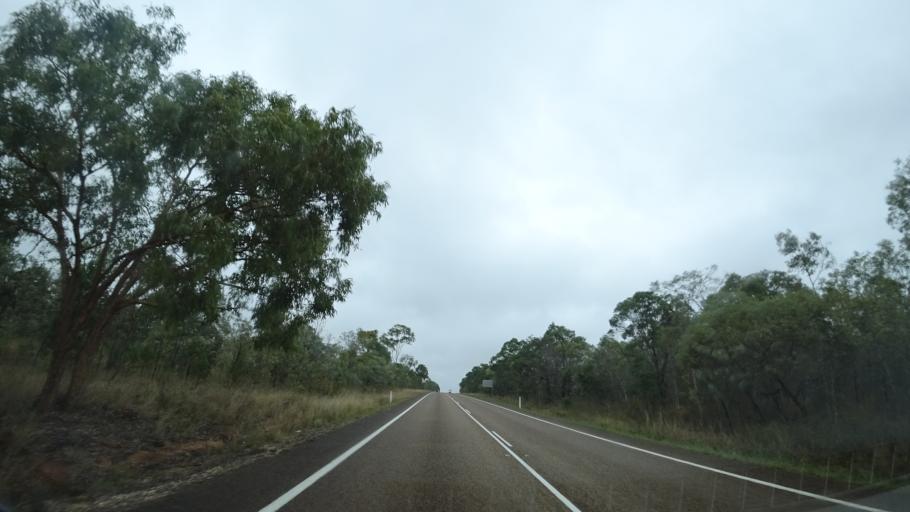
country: AU
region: Queensland
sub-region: Tablelands
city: Ravenshoe
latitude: -17.6949
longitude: 145.1685
